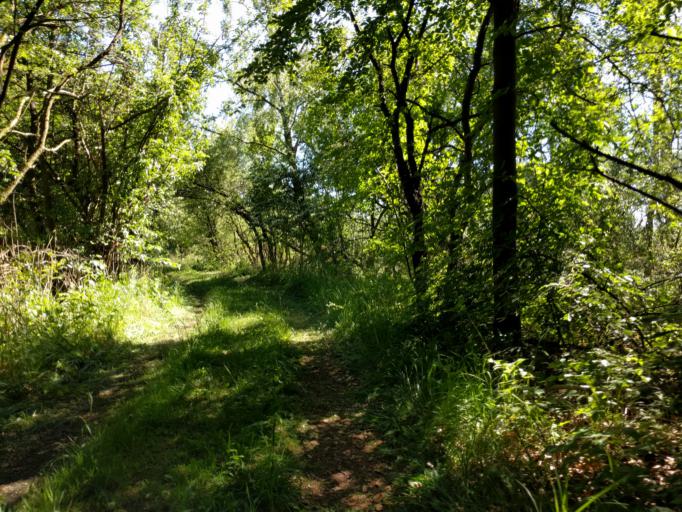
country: DK
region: South Denmark
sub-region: Kerteminde Kommune
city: Langeskov
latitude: 55.3837
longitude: 10.5905
